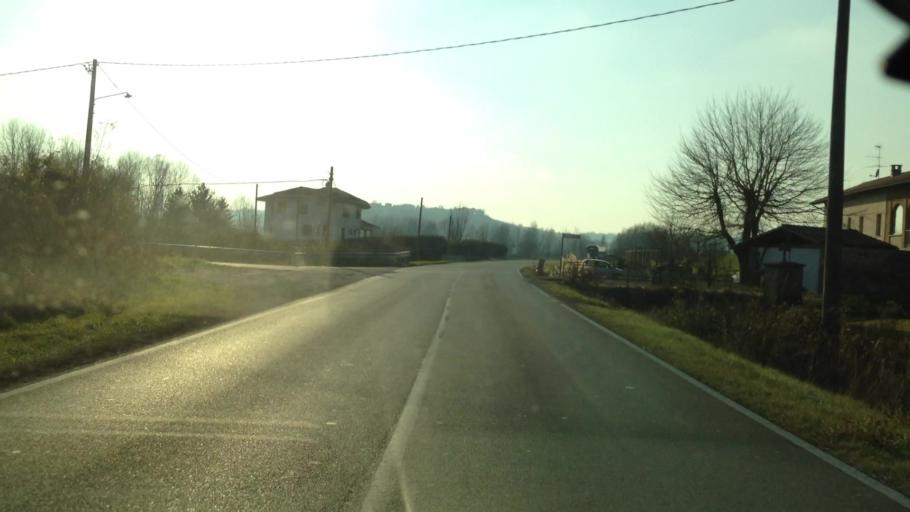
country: IT
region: Piedmont
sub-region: Provincia di Asti
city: Mombercelli
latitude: 44.8209
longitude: 8.2810
